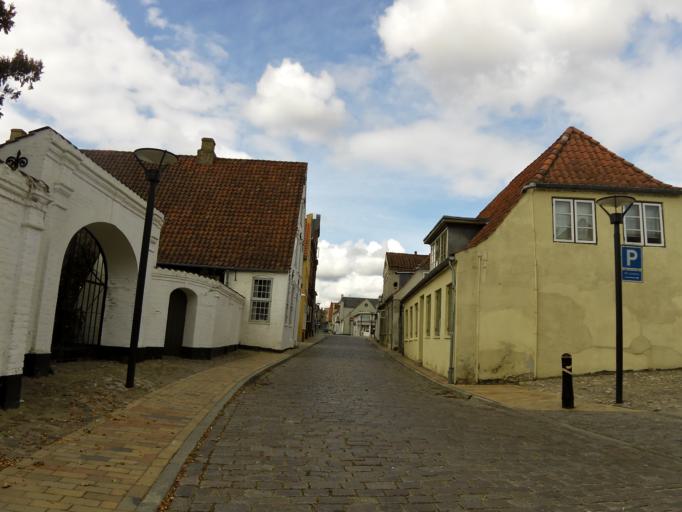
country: DK
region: South Denmark
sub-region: Aabenraa Kommune
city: Aabenraa
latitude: 55.0418
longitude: 9.4159
